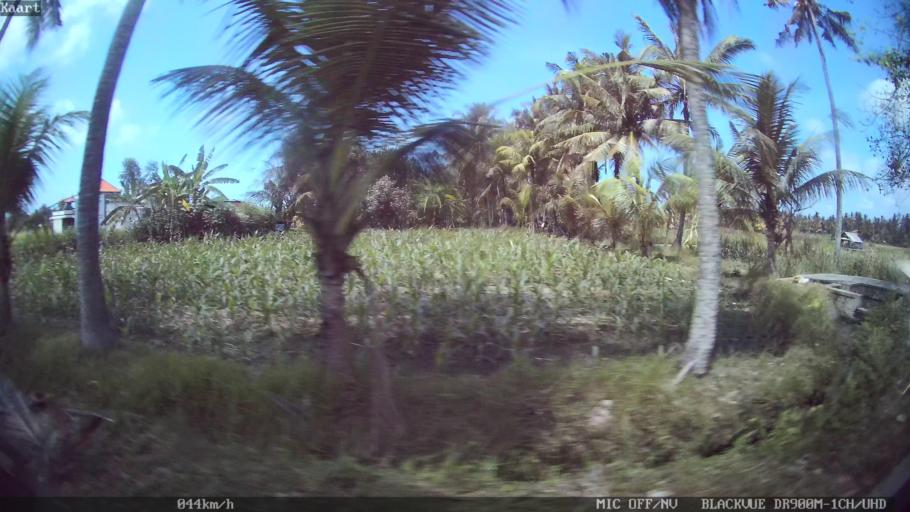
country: ID
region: Bali
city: Banjar Pasekan
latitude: -8.5993
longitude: 115.3056
